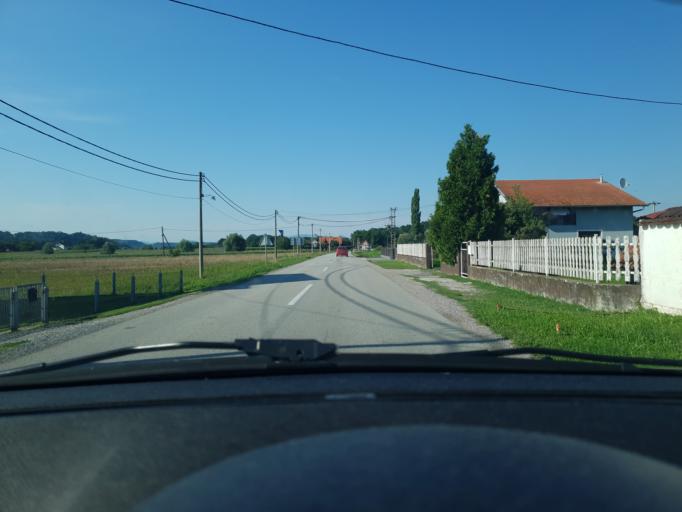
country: HR
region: Zagrebacka
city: Jakovlje
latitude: 45.9503
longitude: 15.8501
